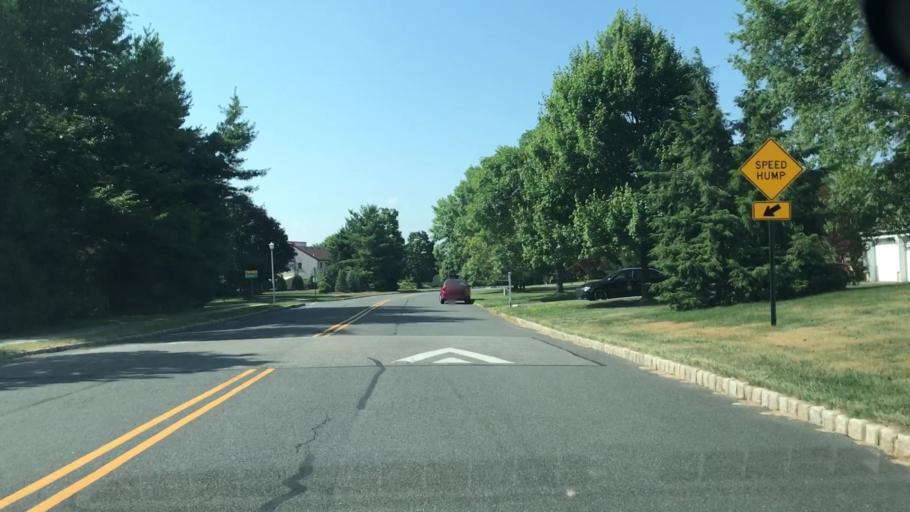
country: US
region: New Jersey
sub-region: Hunterdon County
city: Flemington
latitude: 40.4996
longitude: -74.8446
